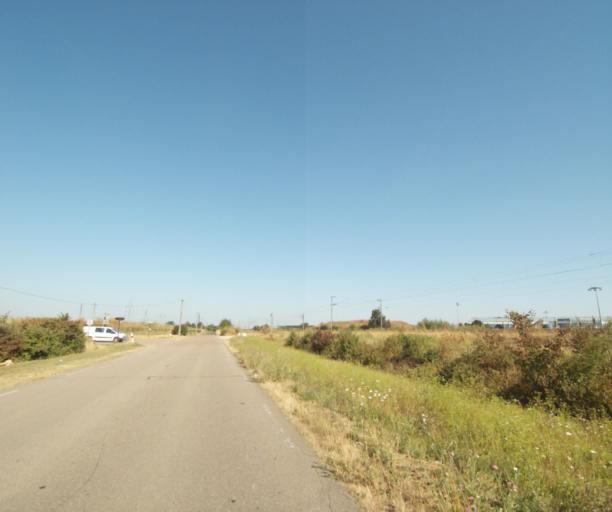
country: FR
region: Ile-de-France
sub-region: Departement de Seine-et-Marne
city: Moissy-Cramayel
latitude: 48.6098
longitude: 2.5869
